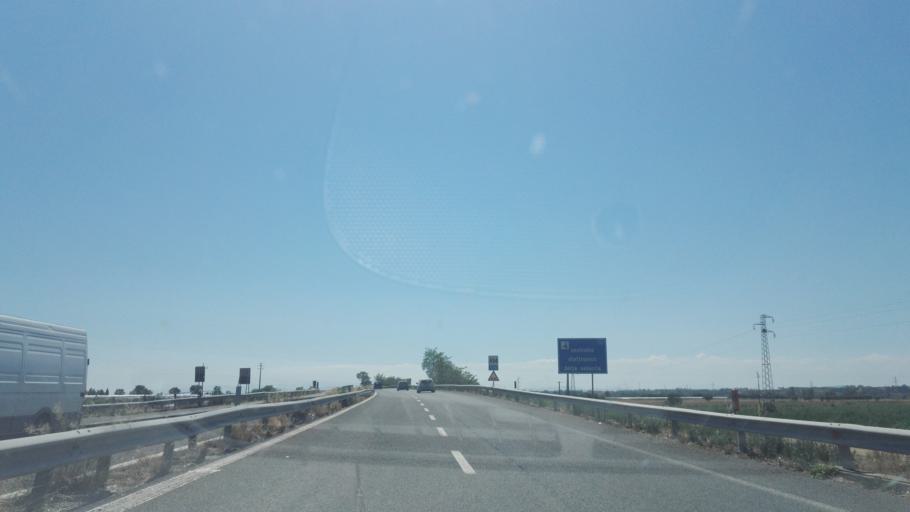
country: IT
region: Apulia
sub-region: Provincia di Taranto
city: Marina di Ginosa
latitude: 40.4308
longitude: 16.8302
